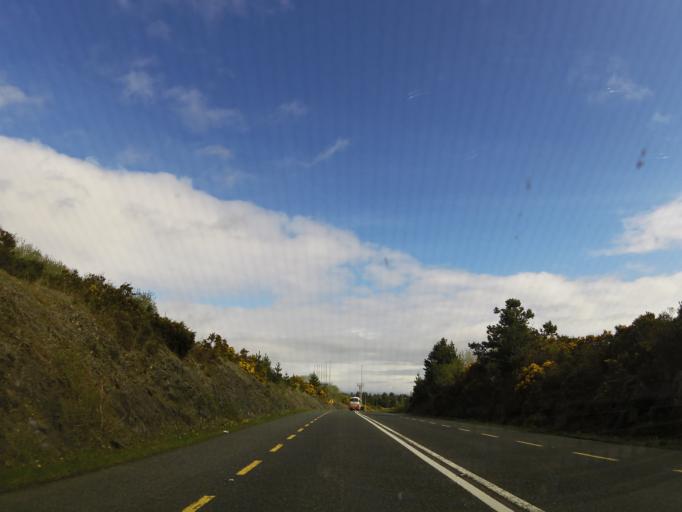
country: IE
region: Connaught
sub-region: Maigh Eo
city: Ballyhaunis
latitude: 53.9106
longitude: -8.7932
